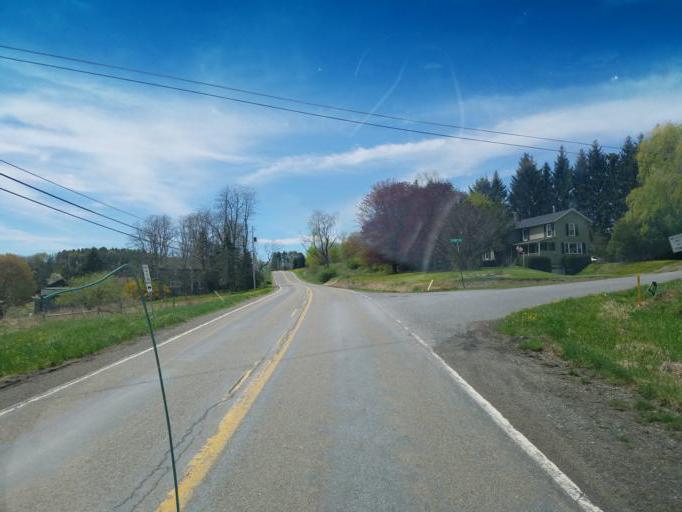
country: US
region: Pennsylvania
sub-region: Tioga County
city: Wellsboro
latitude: 41.7076
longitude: -77.3868
